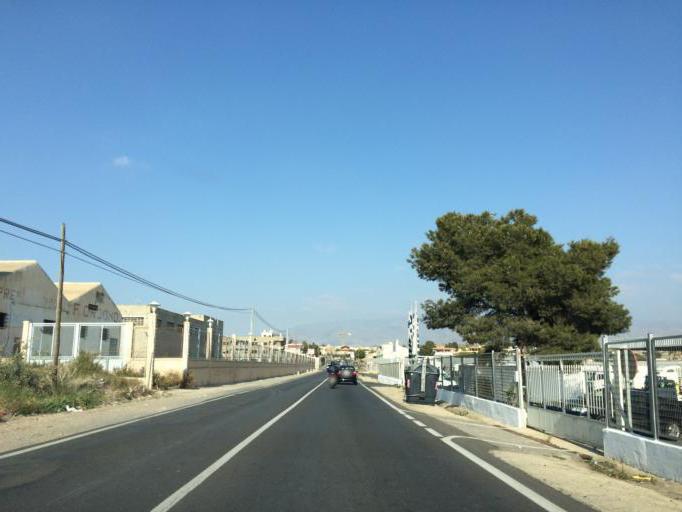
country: ES
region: Andalusia
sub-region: Provincia de Almeria
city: Huercal de Almeria
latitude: 36.8592
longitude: -2.4197
